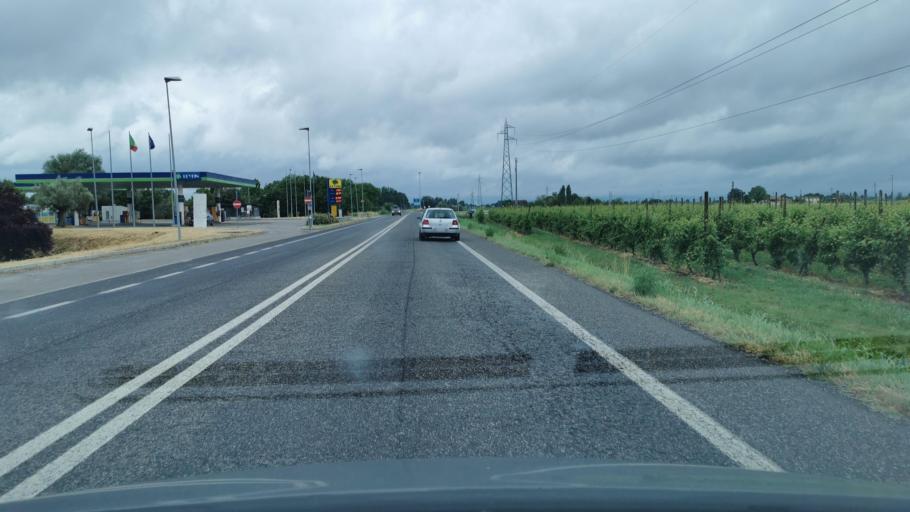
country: IT
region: Emilia-Romagna
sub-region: Provincia di Ravenna
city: Granarolo
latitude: 44.3662
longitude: 11.9368
